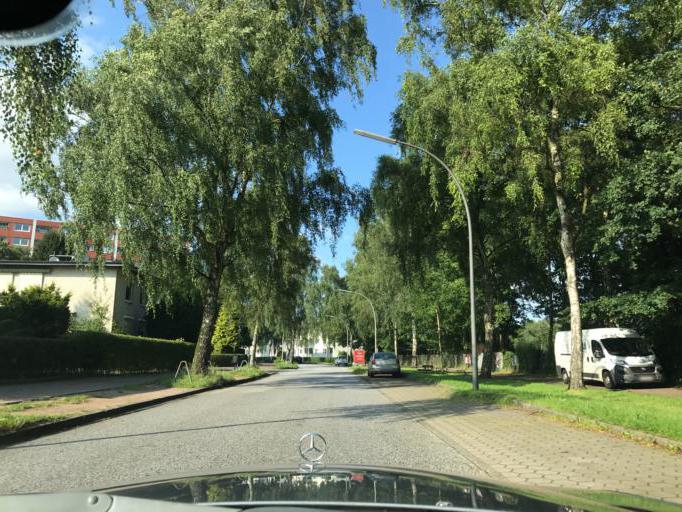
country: DE
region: Hamburg
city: Wandsbek
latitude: 53.5554
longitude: 10.1056
